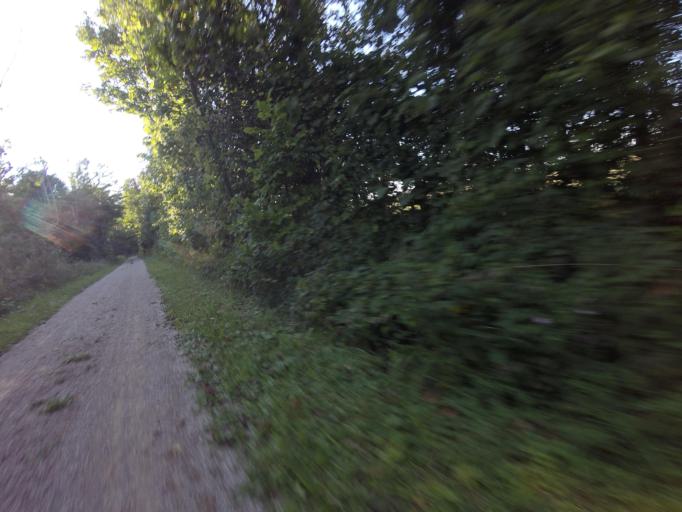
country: CA
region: Ontario
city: Goderich
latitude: 43.7577
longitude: -81.6845
